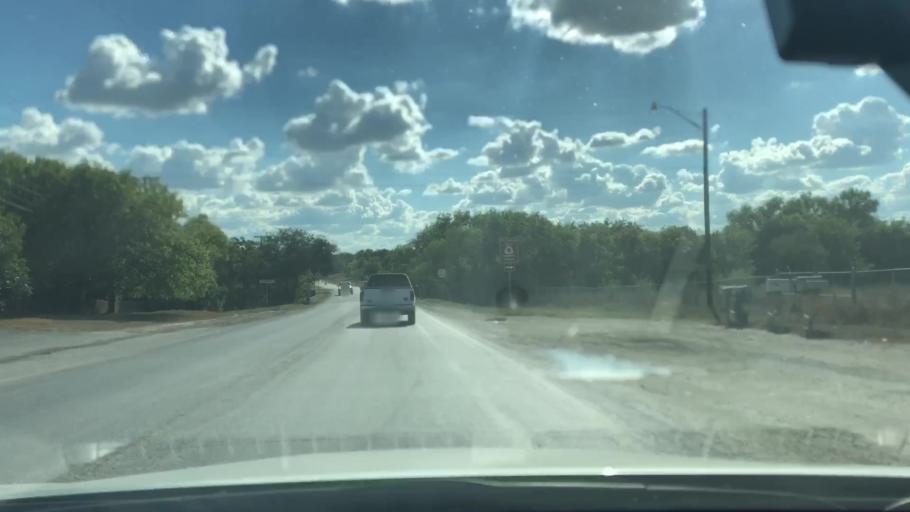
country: US
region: Texas
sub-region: Comal County
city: New Braunfels
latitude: 29.6658
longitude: -98.1716
